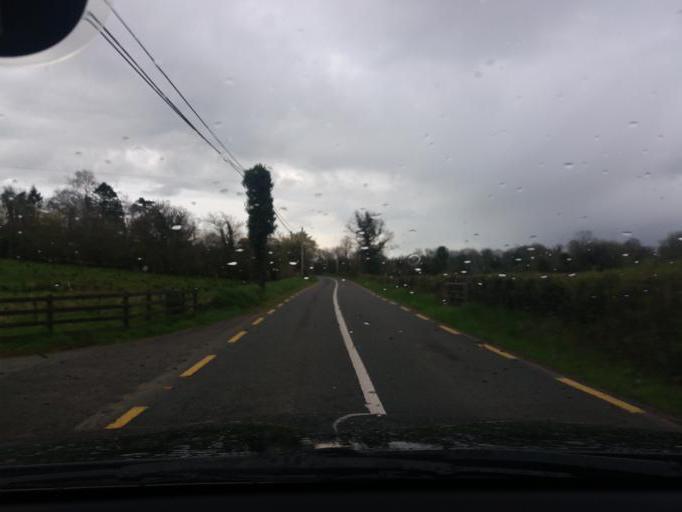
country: IE
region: Ulster
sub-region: An Cabhan
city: Ballyconnell
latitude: 54.1473
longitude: -7.7074
